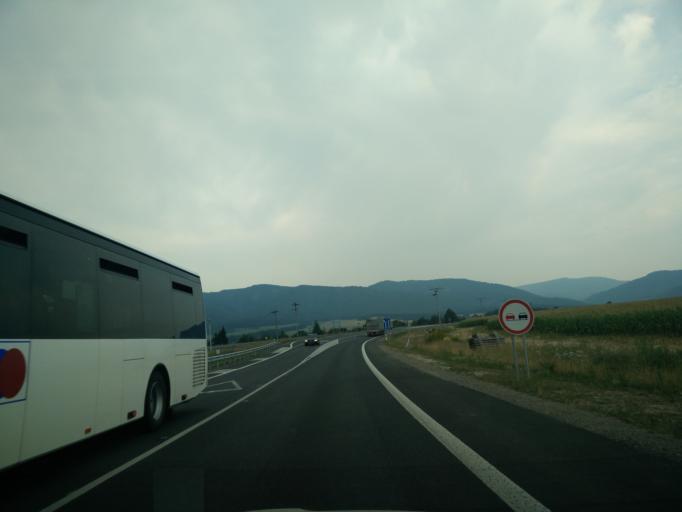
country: SK
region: Banskobystricky
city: Ziar nad Hronom
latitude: 48.6206
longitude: 18.8008
